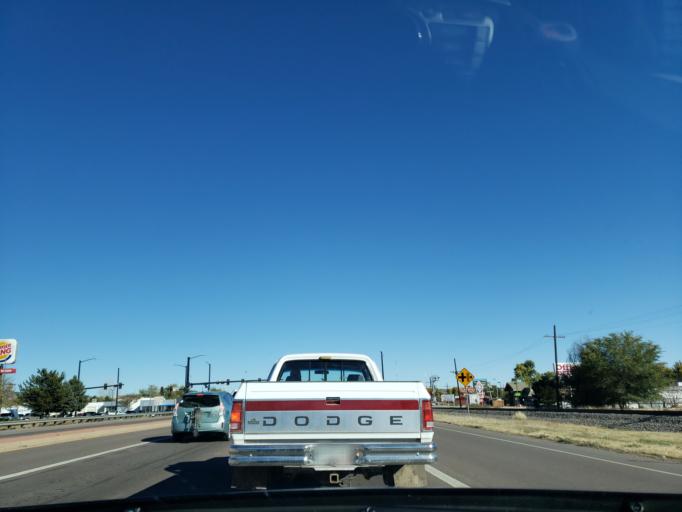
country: US
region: Colorado
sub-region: Fremont County
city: Lincoln Park
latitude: 38.4479
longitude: -105.2083
